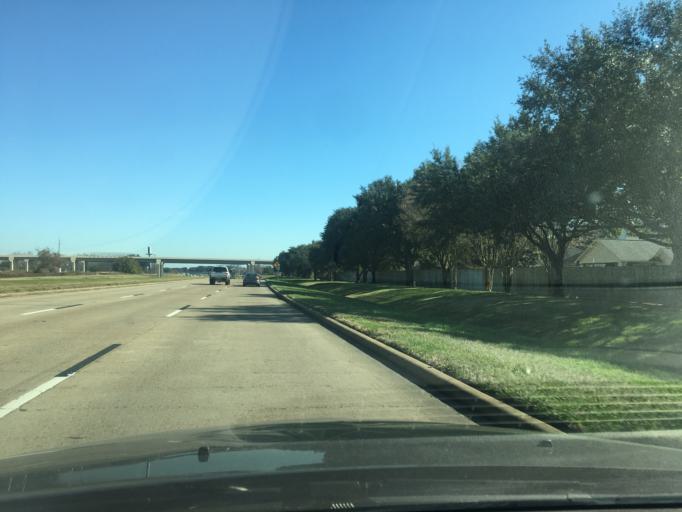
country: US
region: Texas
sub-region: Fort Bend County
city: New Territory
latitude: 29.6012
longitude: -95.6890
